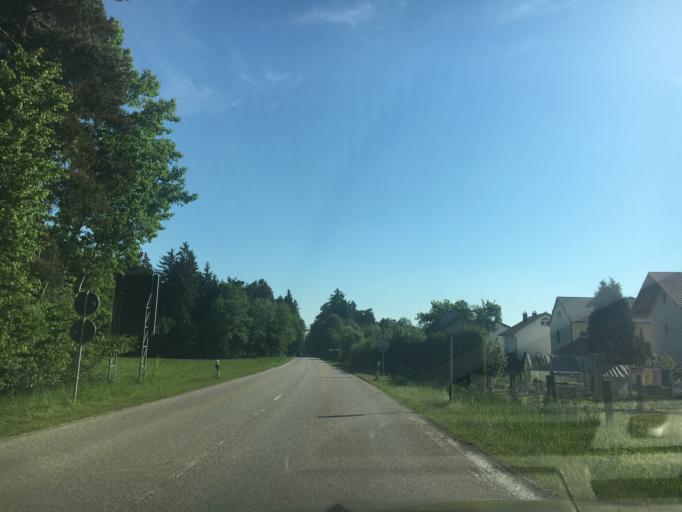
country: DE
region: Bavaria
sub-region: Upper Bavaria
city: Garching an der Alz
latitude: 48.1397
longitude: 12.5992
